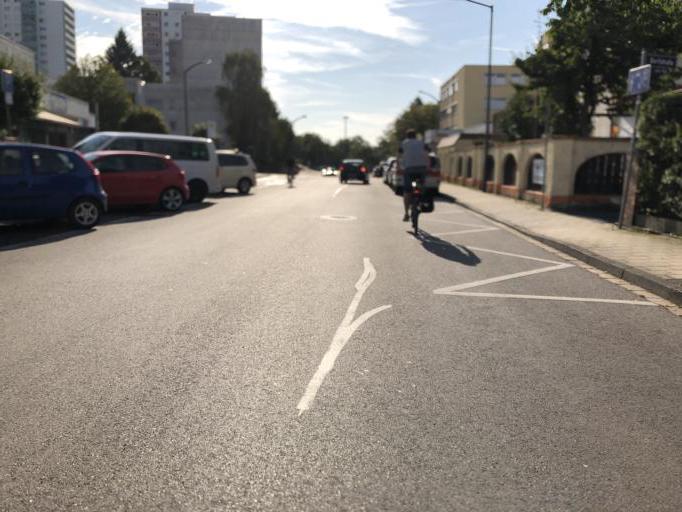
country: DE
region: Bavaria
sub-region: Regierungsbezirk Mittelfranken
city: Erlangen
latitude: 49.5899
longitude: 10.9678
